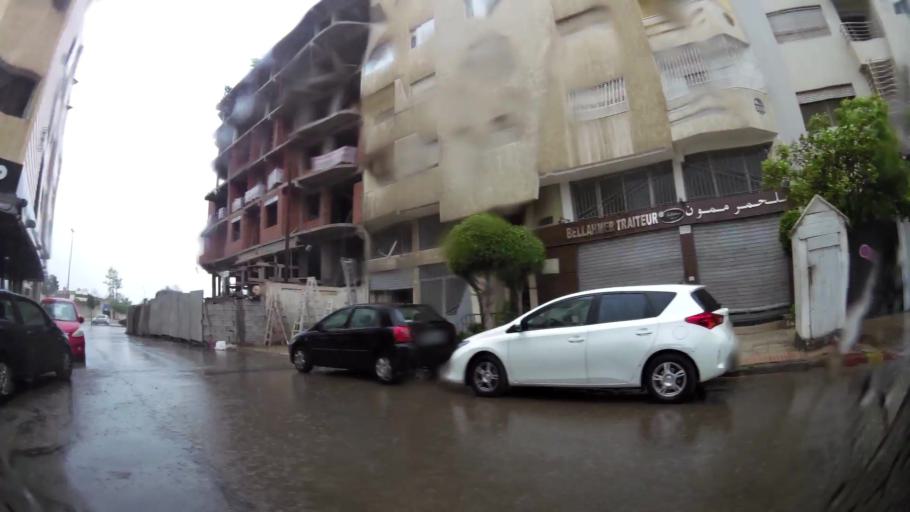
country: MA
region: Grand Casablanca
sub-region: Casablanca
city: Casablanca
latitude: 33.5740
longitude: -7.6310
